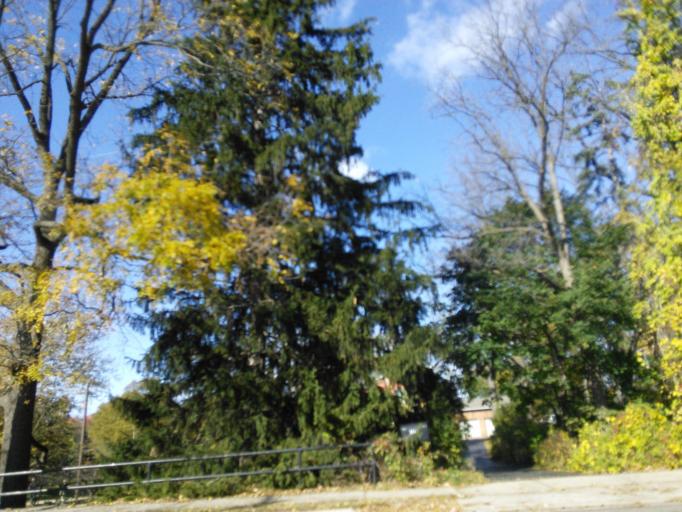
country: US
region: Michigan
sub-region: Washtenaw County
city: Ann Arbor
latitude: 42.2763
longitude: -83.7660
